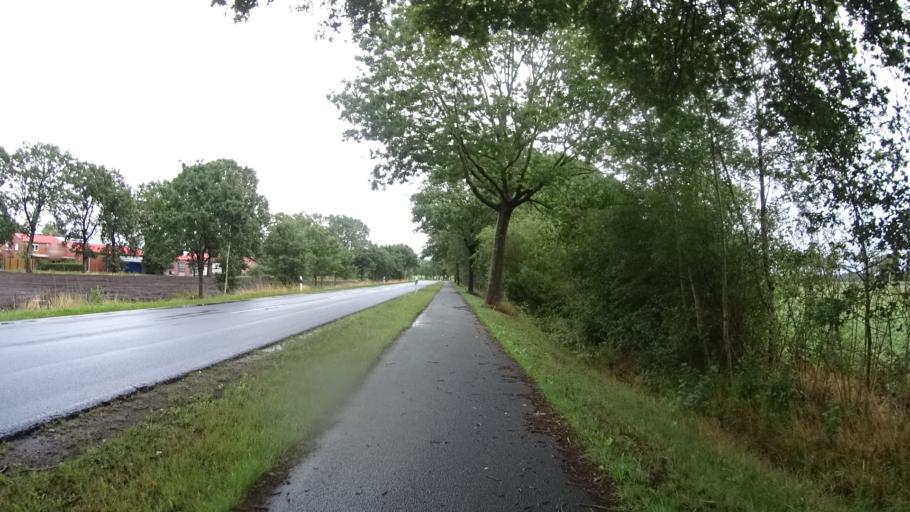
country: DE
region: Lower Saxony
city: Schwerinsdorf
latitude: 53.3377
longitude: 7.6895
